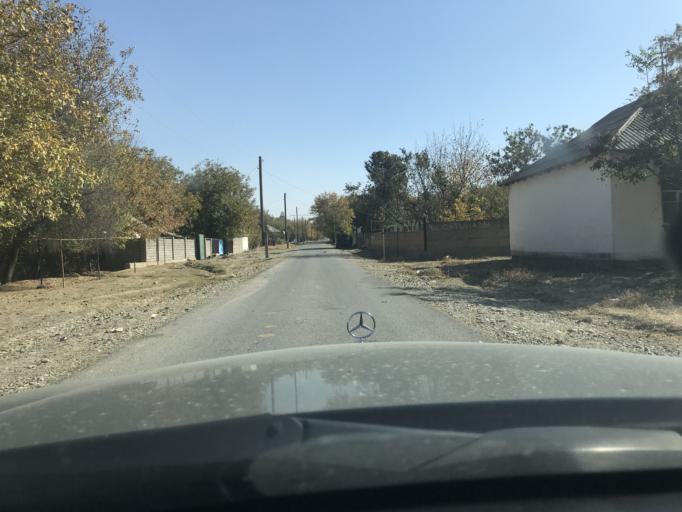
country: KZ
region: Ongtustik Qazaqstan
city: Sastobe
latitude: 42.5444
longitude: 69.9307
